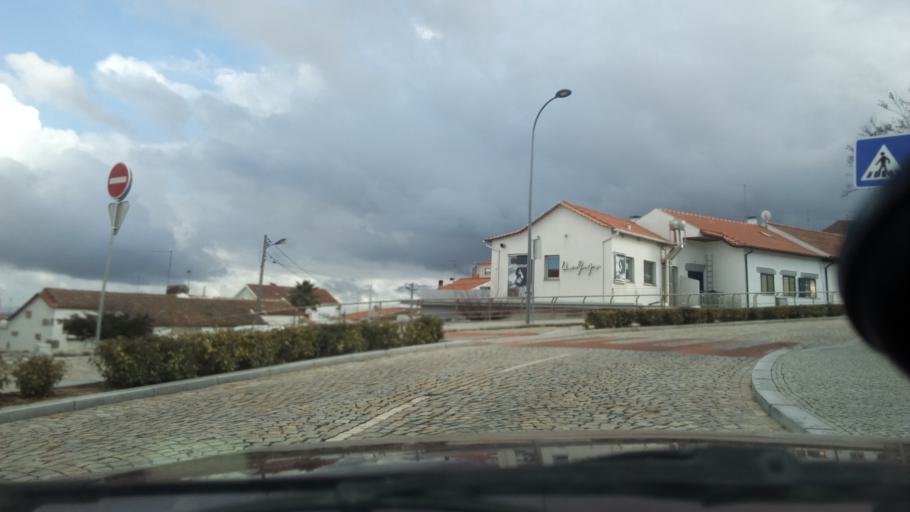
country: PT
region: Guarda
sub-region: Guarda
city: Guarda
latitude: 40.5343
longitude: -7.2631
